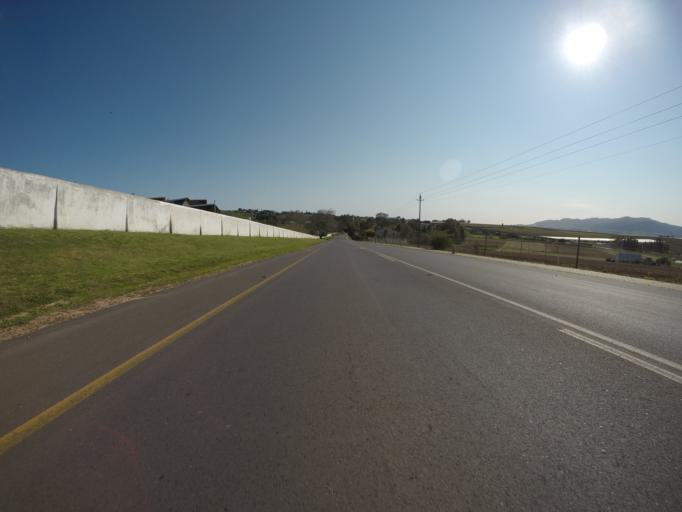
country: ZA
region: Western Cape
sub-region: Cape Winelands District Municipality
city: Noorder-Paarl
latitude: -33.6708
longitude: 18.9217
